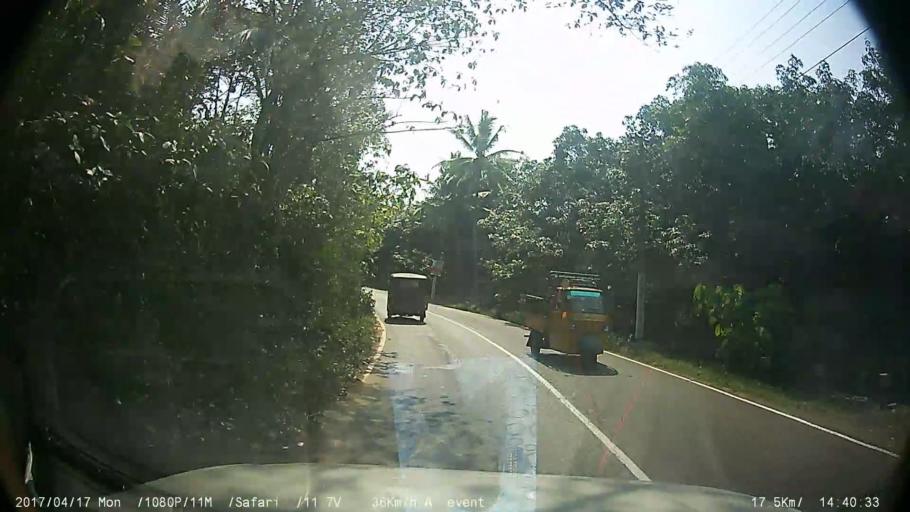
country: IN
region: Kerala
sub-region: Ernakulam
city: Piravam
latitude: 9.8314
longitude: 76.5110
